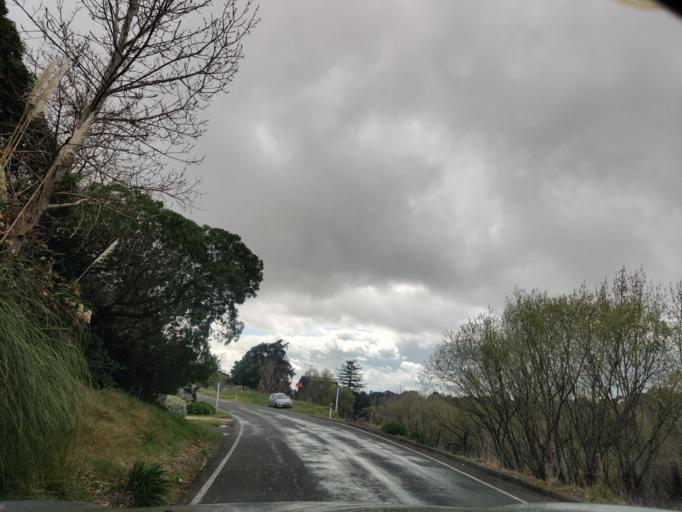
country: NZ
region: Hawke's Bay
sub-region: Hastings District
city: Hastings
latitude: -39.6853
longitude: 176.8984
